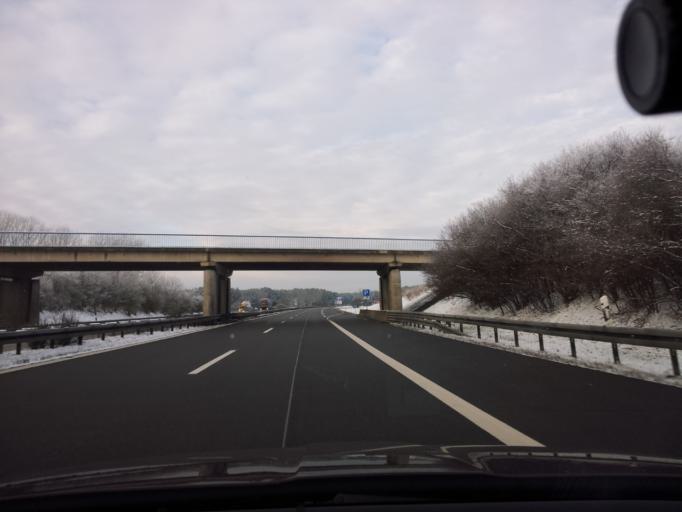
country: DE
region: Mecklenburg-Vorpommern
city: Neustadt-Glewe
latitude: 53.3697
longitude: 11.6576
